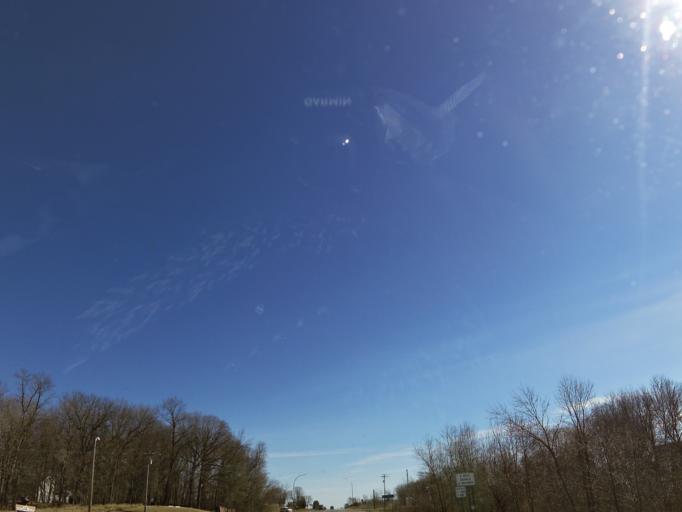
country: US
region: Minnesota
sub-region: Wright County
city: Buffalo
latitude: 45.1460
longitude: -93.8385
